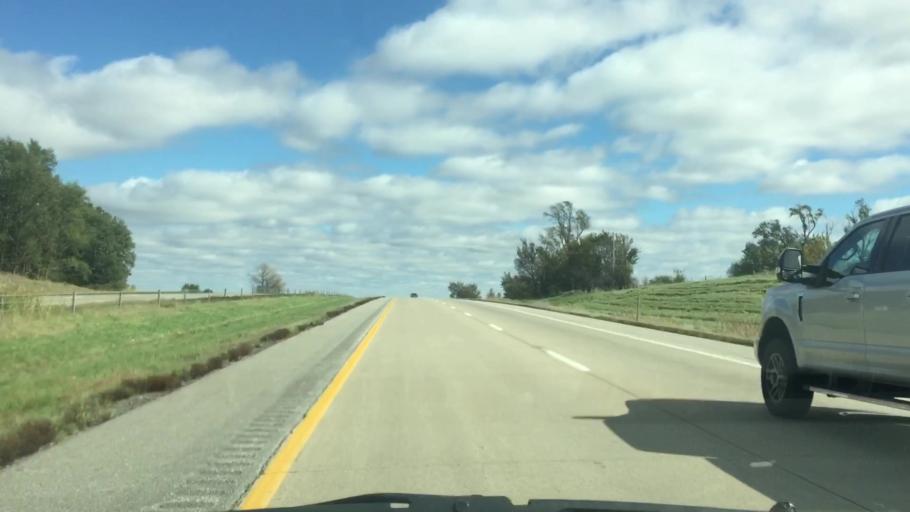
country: US
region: Iowa
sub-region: Poweshiek County
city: Brooklyn
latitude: 41.6954
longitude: -92.3403
